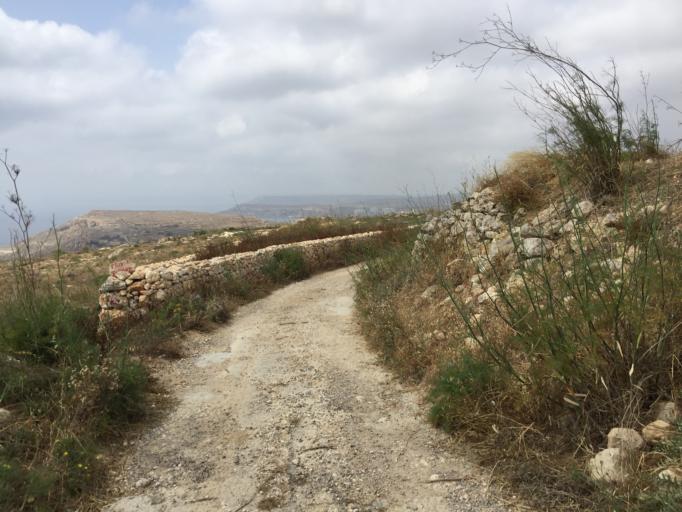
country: MT
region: L-Imgarr
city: Imgarr
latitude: 35.9021
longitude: 14.3461
